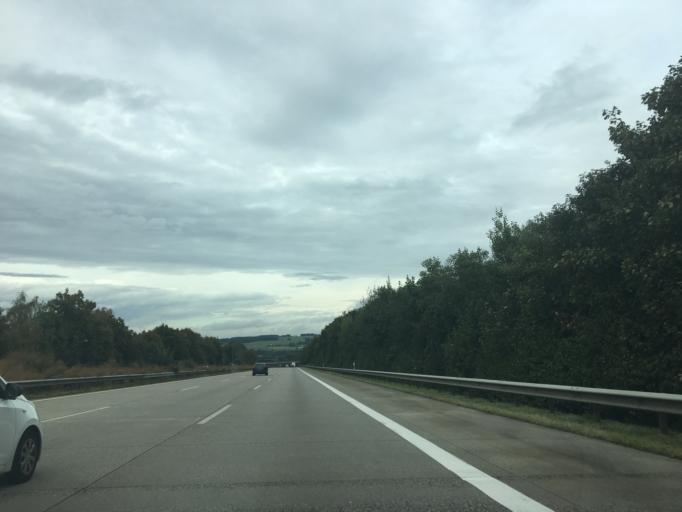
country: DE
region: Rheinland-Pfalz
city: Breitscheid
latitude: 50.6053
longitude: 7.4297
